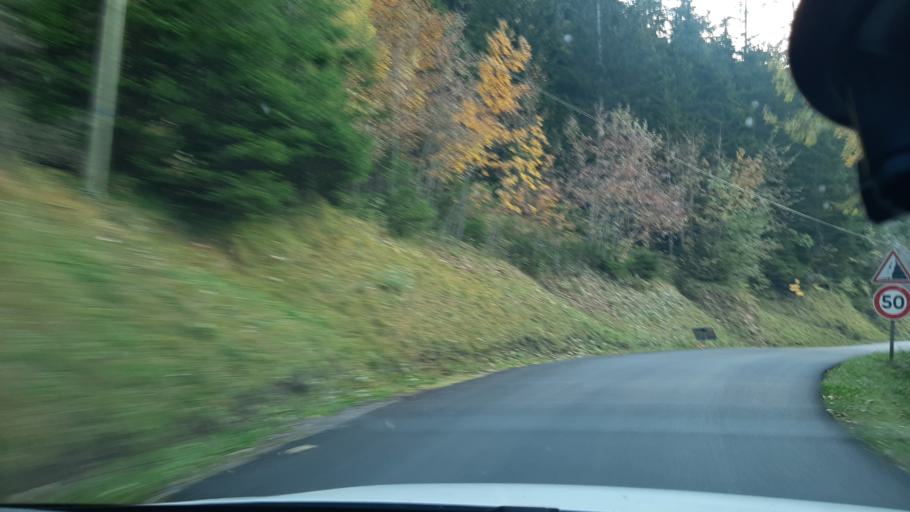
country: FR
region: Rhone-Alpes
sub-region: Departement de la Savoie
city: Saint-Jean-de-Maurienne
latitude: 45.1970
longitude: 6.3044
